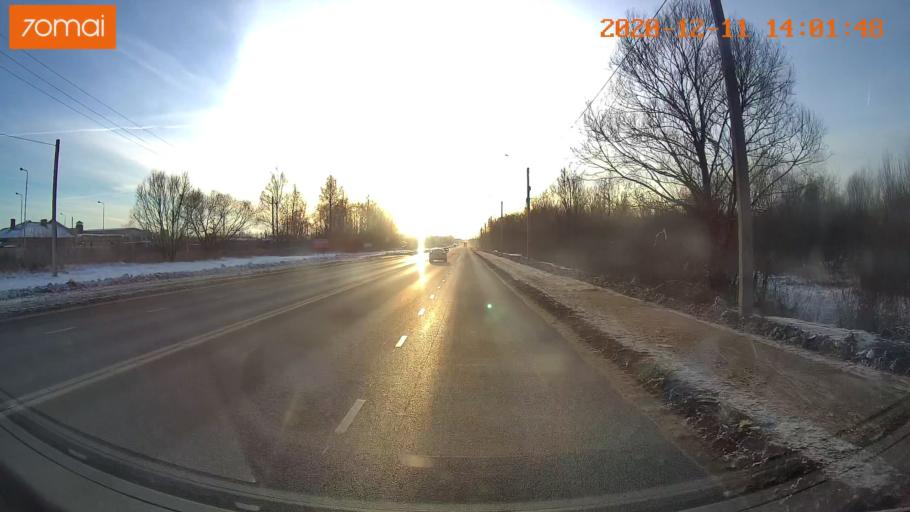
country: RU
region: Kostroma
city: Oktyabr'skiy
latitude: 57.7799
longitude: 41.0326
